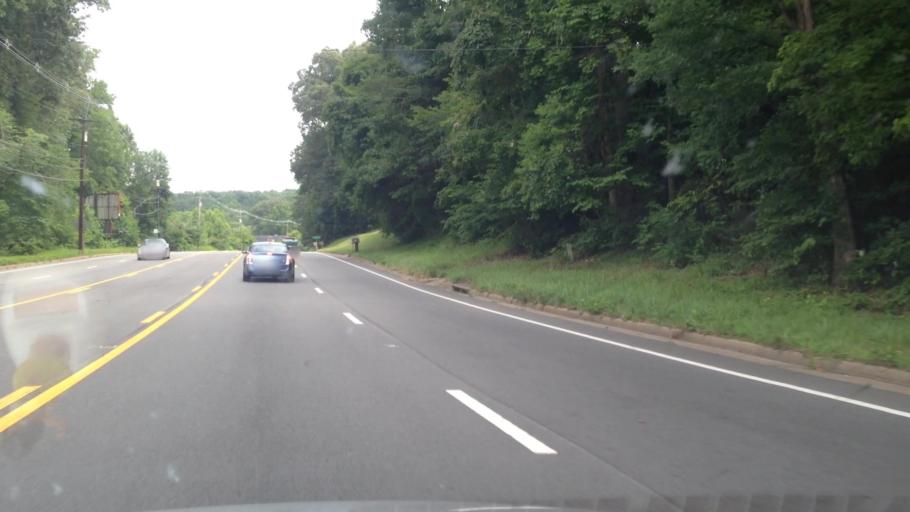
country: US
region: Virginia
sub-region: Pittsylvania County
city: Mount Hermon
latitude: 36.6461
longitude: -79.3813
